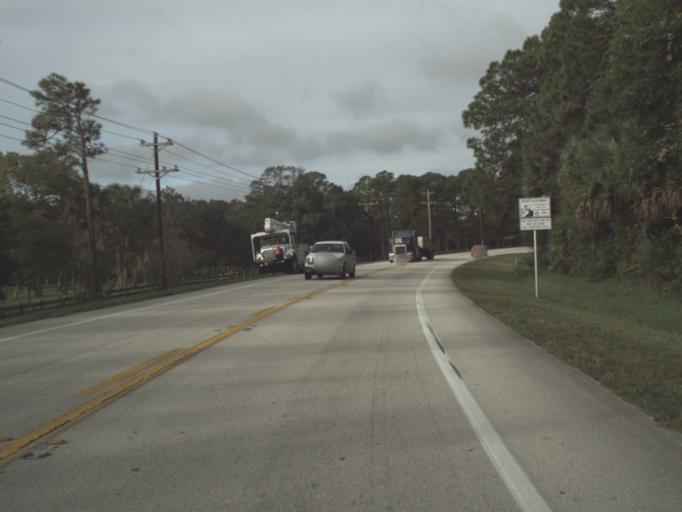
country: US
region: Florida
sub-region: Lee County
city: Fort Myers Shores
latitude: 26.7157
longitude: -81.7702
